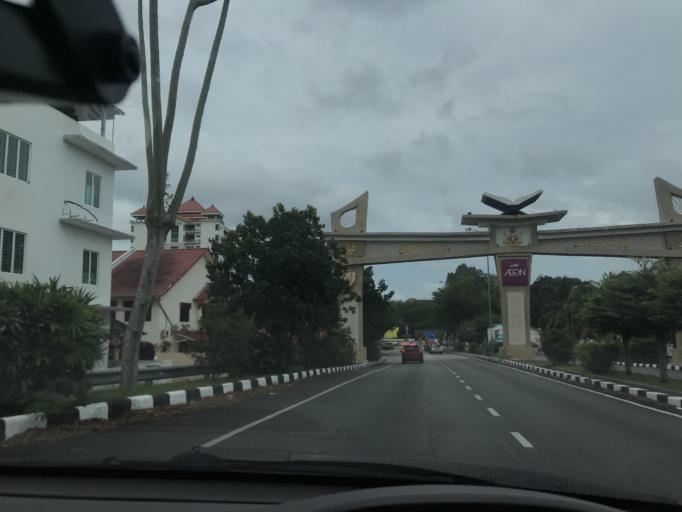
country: MY
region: Kelantan
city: Kota Bharu
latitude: 6.1110
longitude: 102.2365
